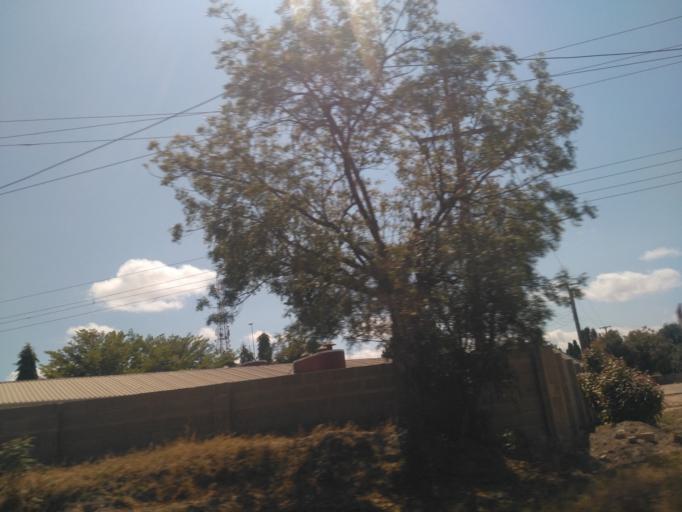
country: TZ
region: Dodoma
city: Dodoma
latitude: -6.1624
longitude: 35.7612
